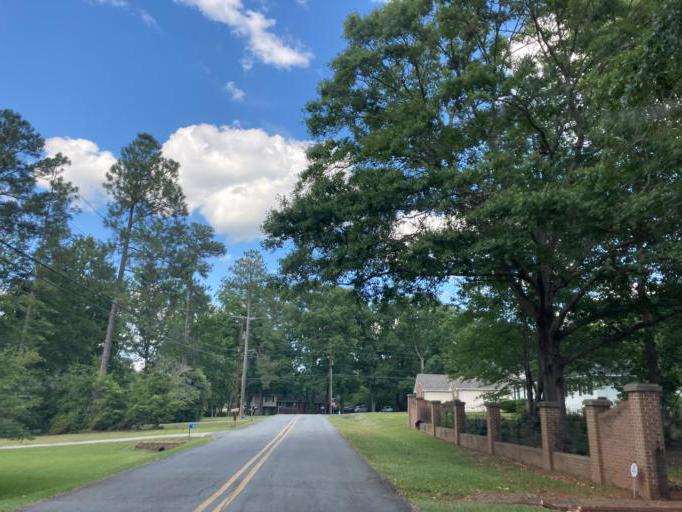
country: US
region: Georgia
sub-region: Jones County
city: Gray
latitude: 33.0042
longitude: -83.5392
